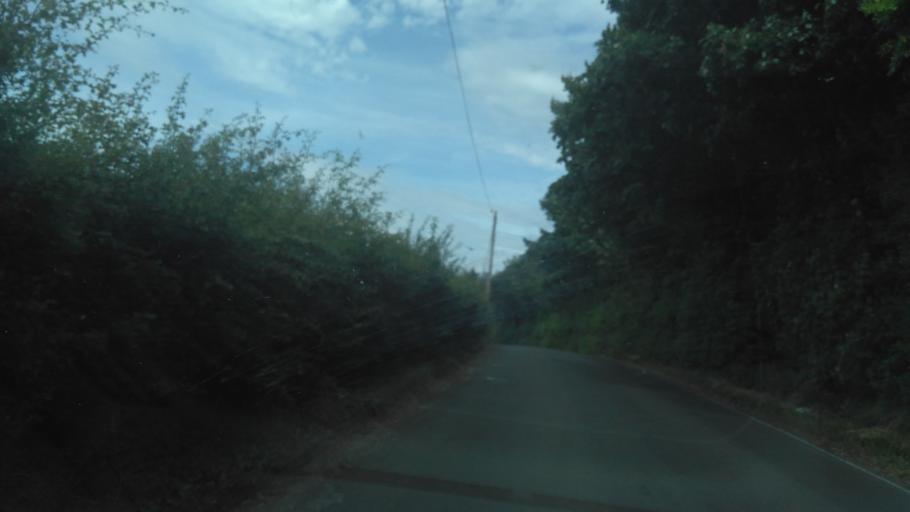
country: GB
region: England
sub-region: Kent
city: Chartham
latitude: 51.2457
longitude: 1.0287
